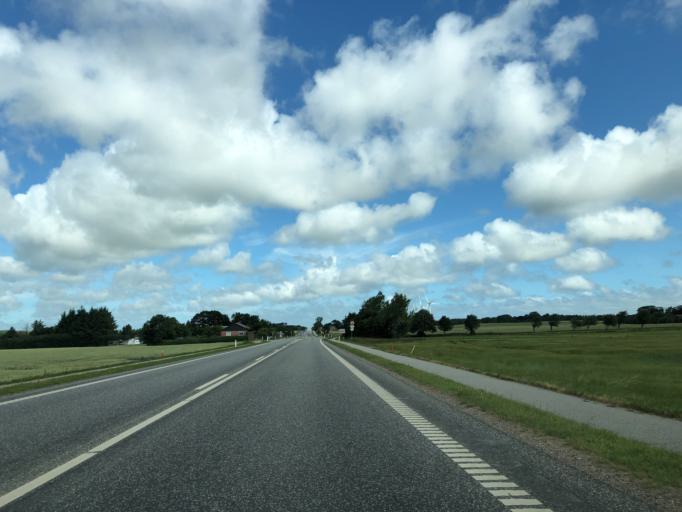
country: DK
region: Central Jutland
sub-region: Holstebro Kommune
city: Holstebro
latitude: 56.4015
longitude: 8.6071
